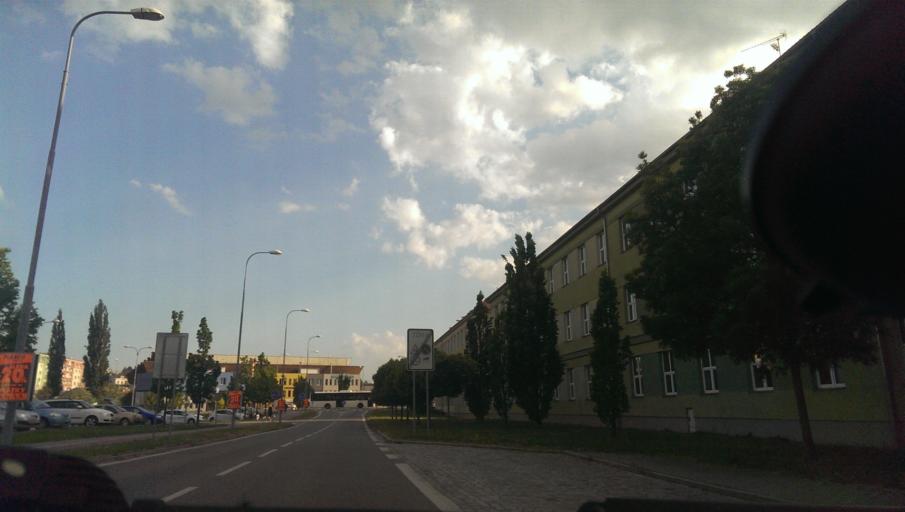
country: CZ
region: Zlin
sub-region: Okres Uherske Hradiste
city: Uherske Hradiste
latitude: 49.0706
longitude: 17.4732
